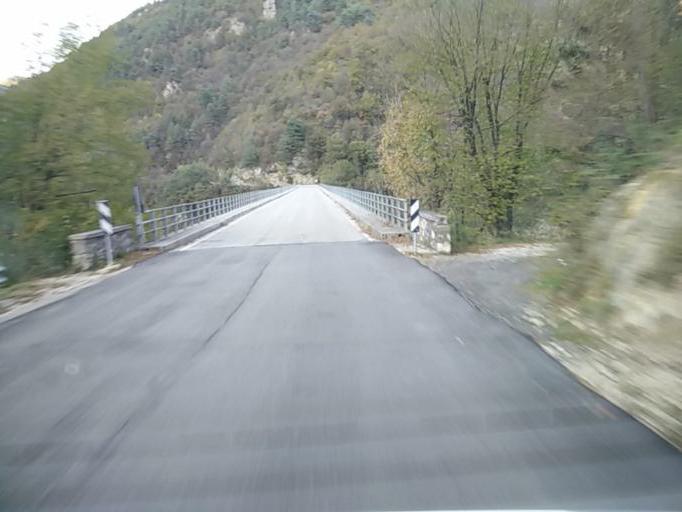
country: IT
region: Lombardy
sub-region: Provincia di Brescia
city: Valvestino
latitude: 45.7208
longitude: 10.6121
